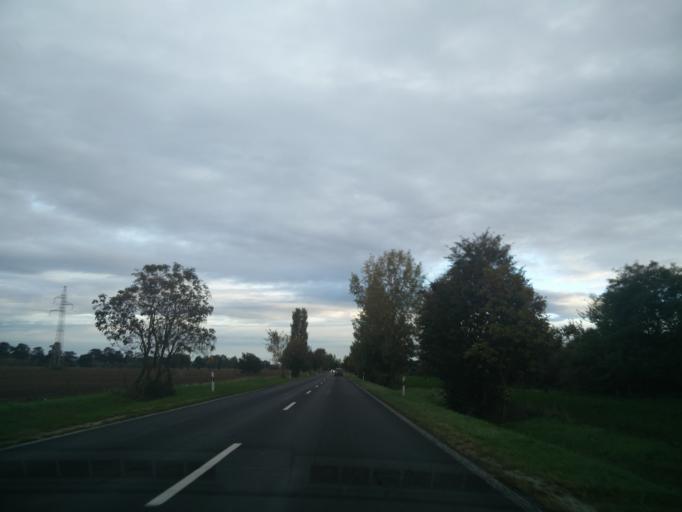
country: HU
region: Zala
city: Keszthely
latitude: 46.7281
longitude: 17.2289
